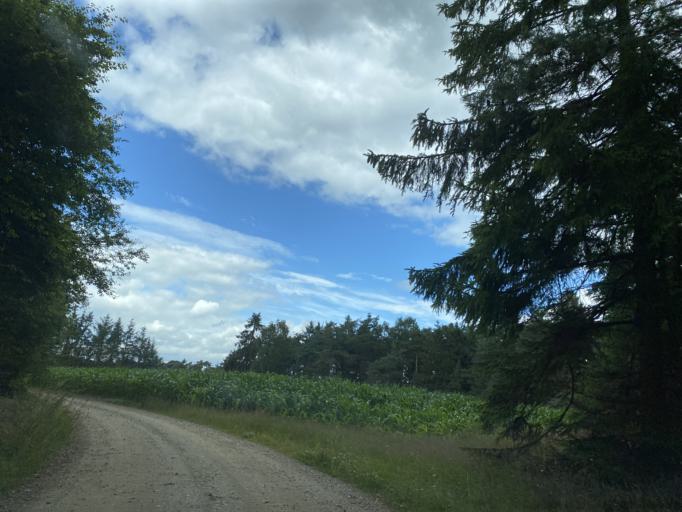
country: DK
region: Central Jutland
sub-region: Viborg Kommune
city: Bjerringbro
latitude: 56.2867
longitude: 9.6555
